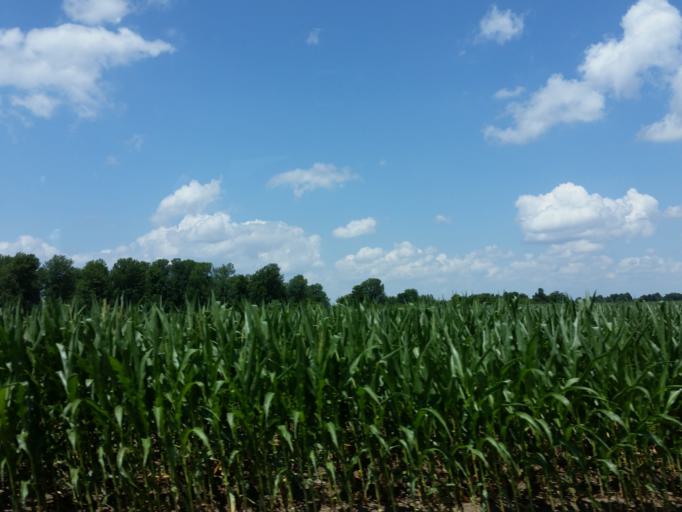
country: US
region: Kentucky
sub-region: Fulton County
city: Hickman
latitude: 36.5415
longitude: -89.3372
